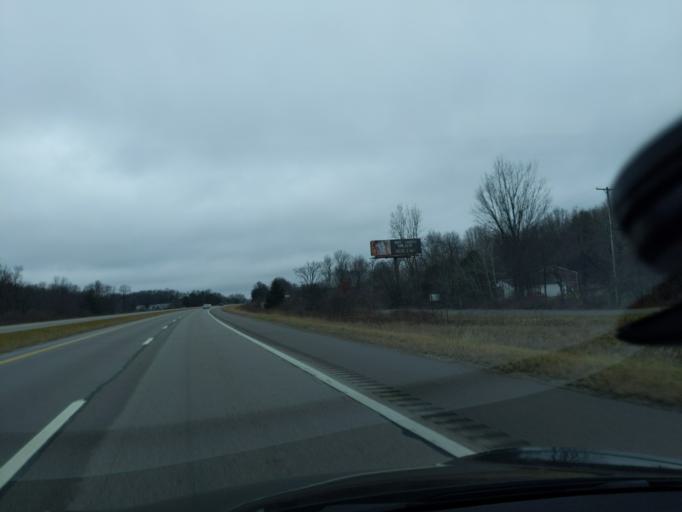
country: US
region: Michigan
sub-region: Ingham County
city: Leslie
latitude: 42.4369
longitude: -84.4428
